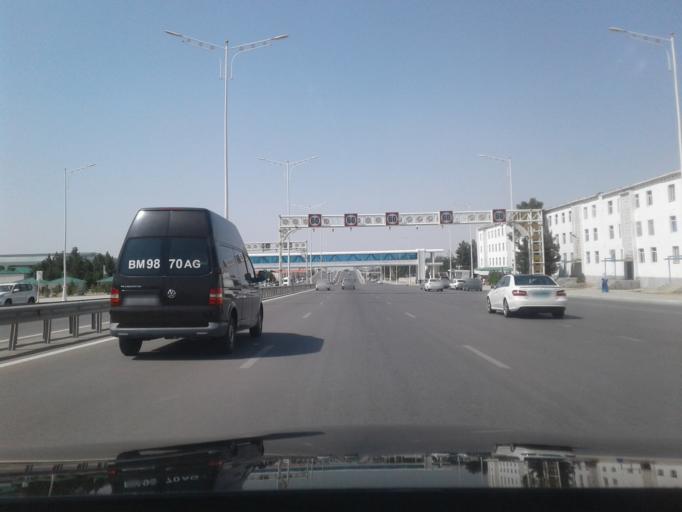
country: TM
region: Ahal
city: Ashgabat
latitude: 37.9137
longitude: 58.4236
